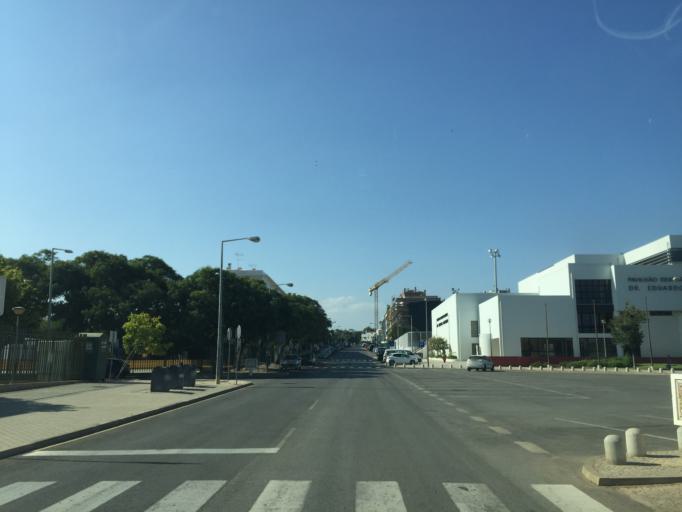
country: PT
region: Faro
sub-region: Tavira
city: Tavira
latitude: 37.1312
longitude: -7.6414
